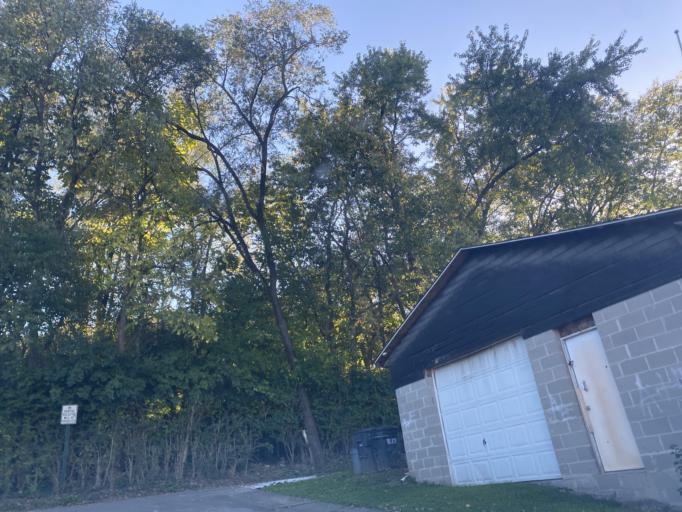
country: US
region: Kentucky
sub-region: Campbell County
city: Dayton
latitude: 39.1140
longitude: -84.4651
